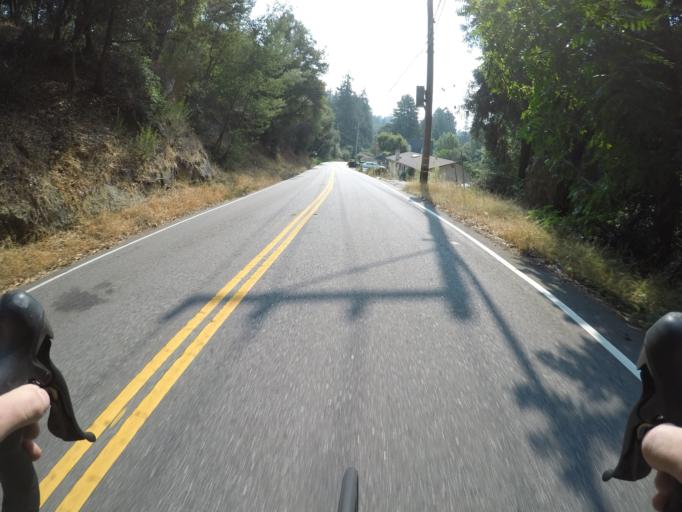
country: US
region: California
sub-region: Santa Cruz County
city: Pasatiempo
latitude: 37.0135
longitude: -122.0141
